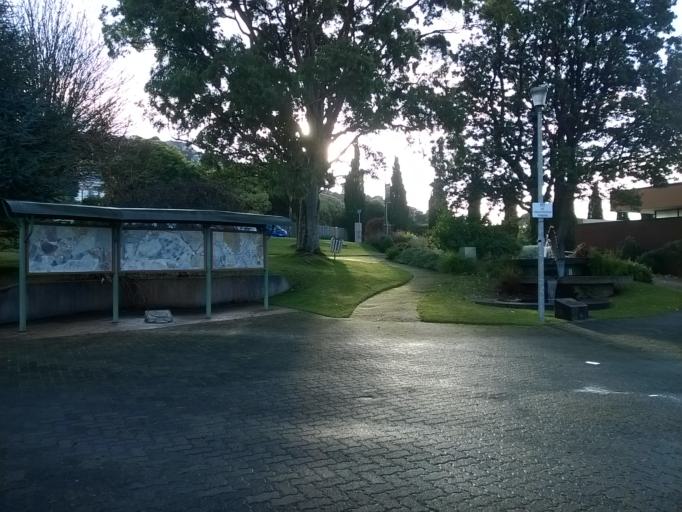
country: AU
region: Tasmania
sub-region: Burnie
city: Burnie
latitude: -41.0515
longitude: 145.9025
